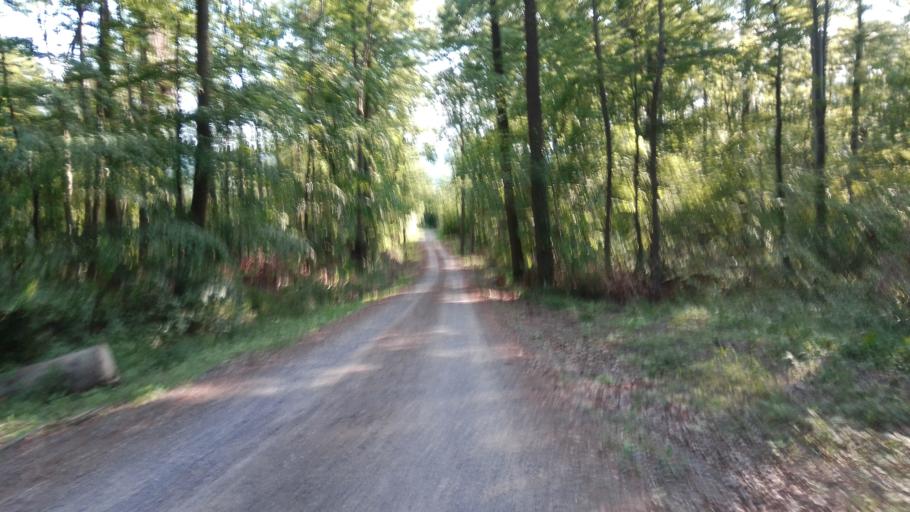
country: DE
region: Lower Saxony
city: Halle
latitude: 52.0015
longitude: 9.5917
